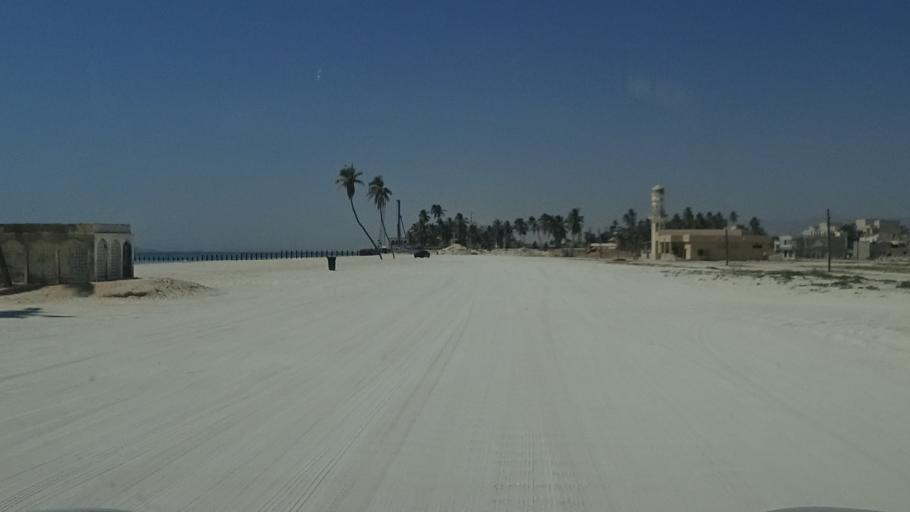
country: OM
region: Zufar
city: Salalah
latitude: 17.0001
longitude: 54.1050
